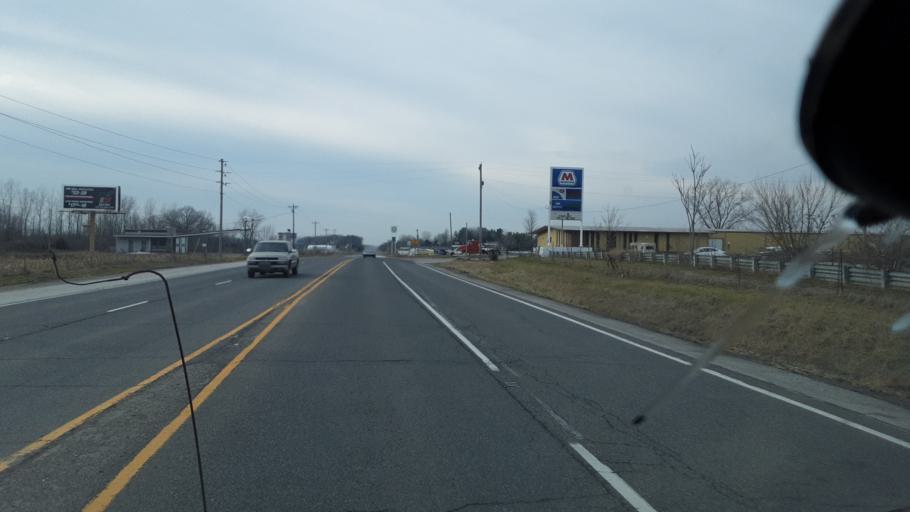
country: US
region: Indiana
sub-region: DeKalb County
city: Waterloo
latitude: 41.4397
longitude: -85.0561
